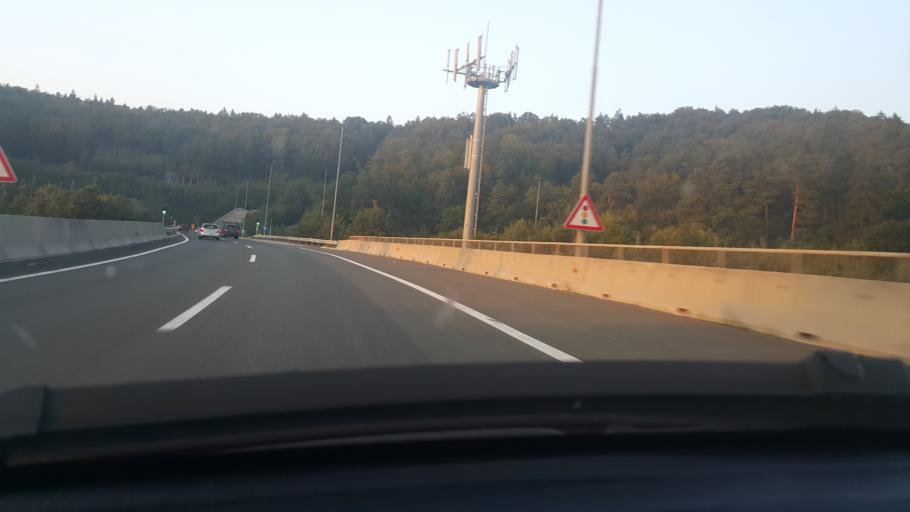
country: SI
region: Skofljica
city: Lavrica
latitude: 46.0143
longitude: 14.5576
